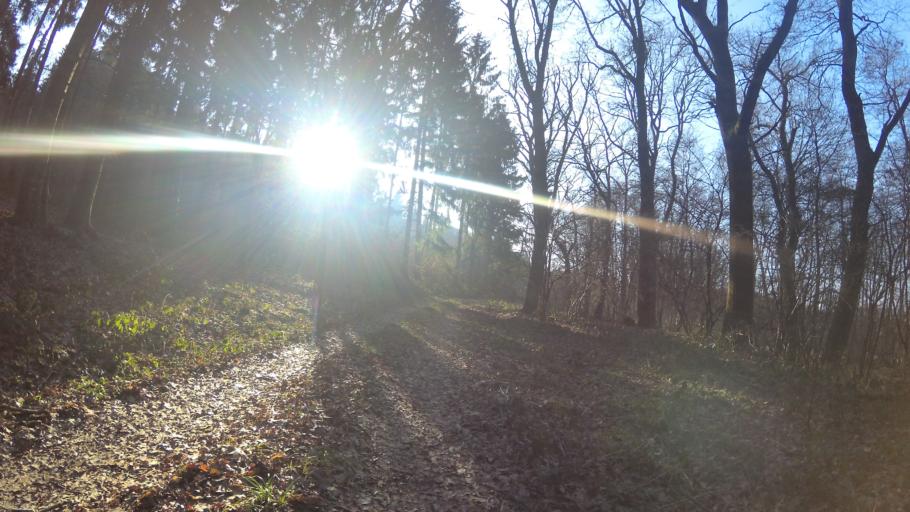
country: DE
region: Saarland
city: Sankt Wendel
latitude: 49.4382
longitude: 7.1987
